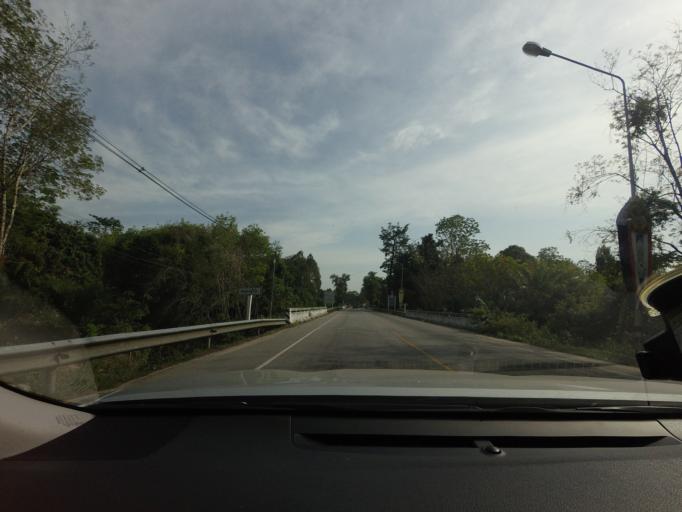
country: TH
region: Narathiwat
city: Ra-ngae
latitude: 6.3273
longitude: 101.7888
